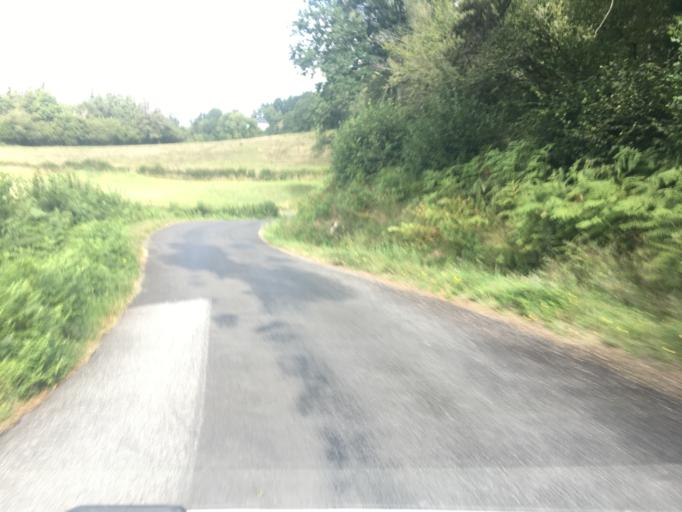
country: FR
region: Auvergne
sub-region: Departement du Cantal
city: Champagnac
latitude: 45.4395
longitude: 2.4041
